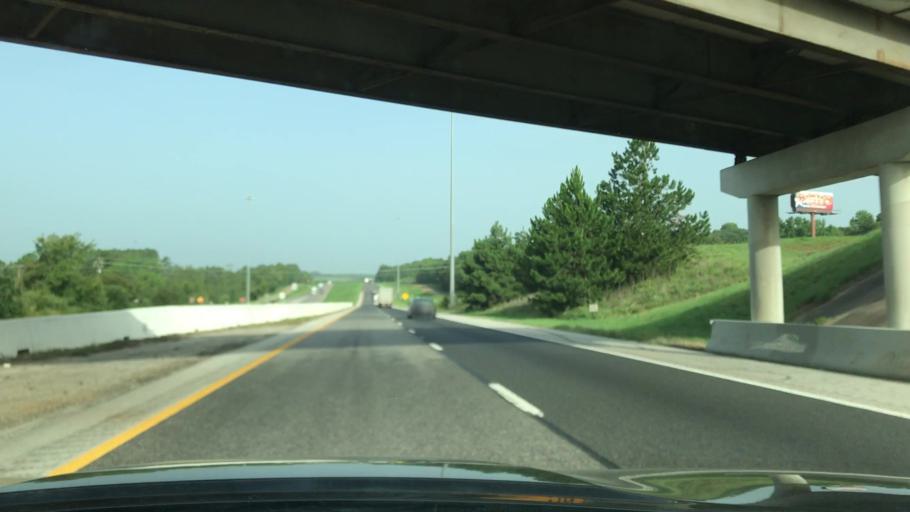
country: US
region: Texas
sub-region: Smith County
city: Tyler
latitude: 32.4532
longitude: -95.2835
